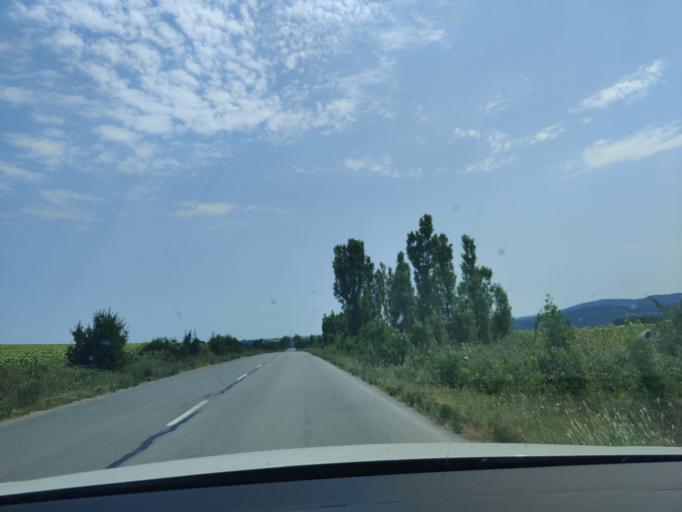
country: BG
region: Vidin
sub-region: Obshtina Ruzhintsi
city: Ruzhintsi
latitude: 43.5710
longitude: 22.8910
